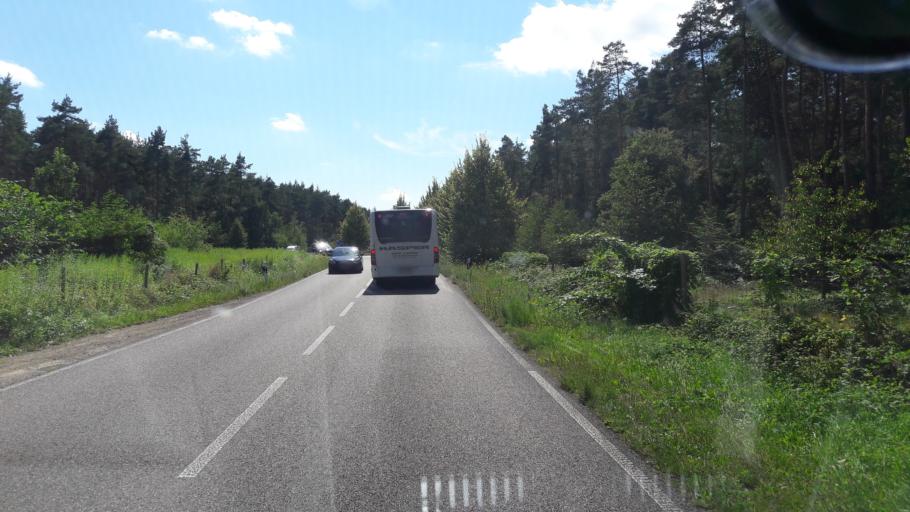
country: DE
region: Baden-Wuerttemberg
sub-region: Karlsruhe Region
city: Linkenheim-Hochstetten
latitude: 49.1465
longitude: 8.4507
